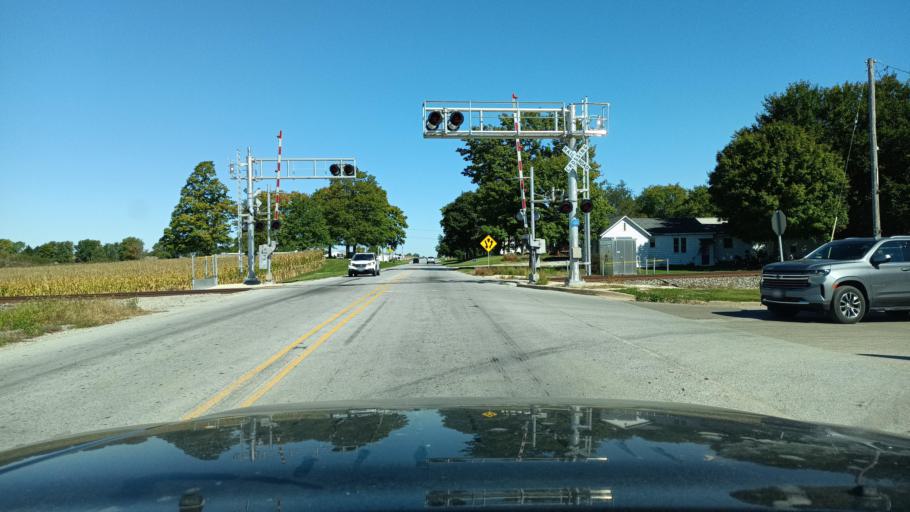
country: US
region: Illinois
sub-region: Champaign County
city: Philo
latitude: 40.0066
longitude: -88.1614
